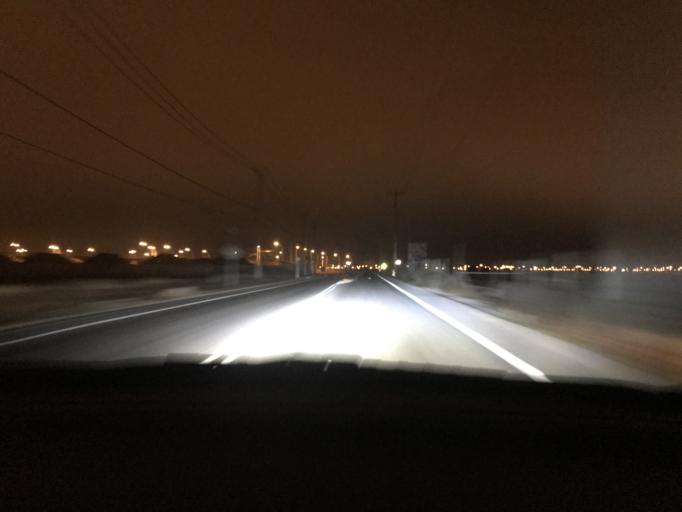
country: CL
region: Coquimbo
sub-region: Provincia de Elqui
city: La Serena
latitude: -29.9229
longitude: -71.2258
